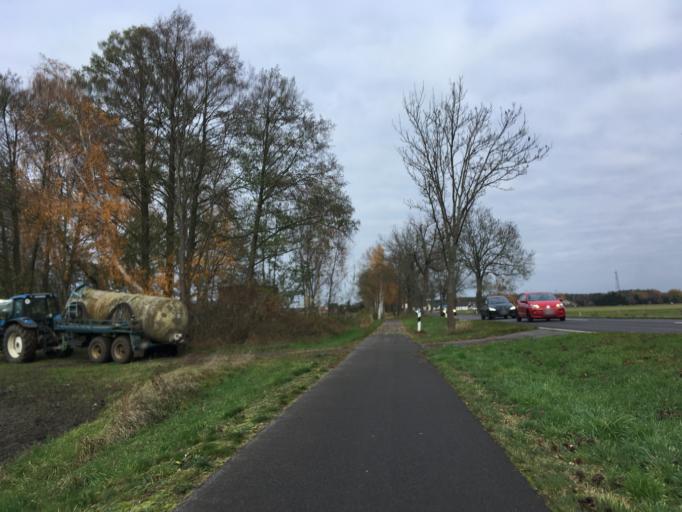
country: DE
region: Brandenburg
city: Peitz
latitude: 51.8764
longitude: 14.4188
